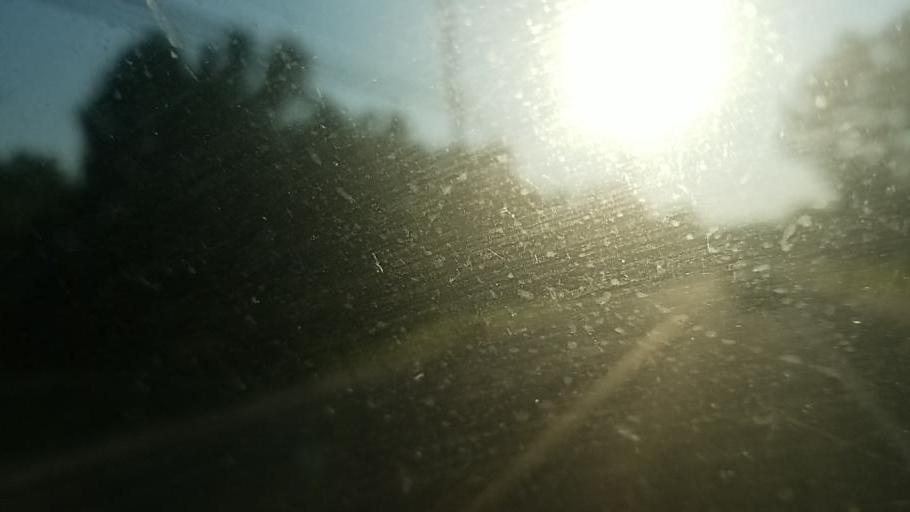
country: US
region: Delaware
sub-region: Sussex County
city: Selbyville
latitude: 38.4566
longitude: -75.2183
